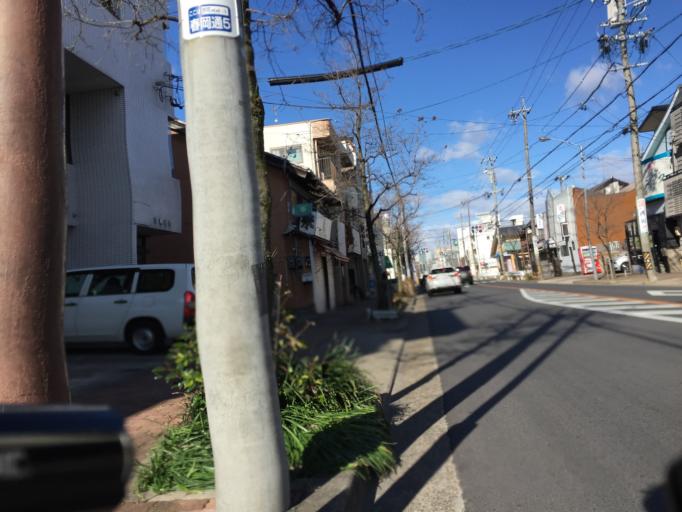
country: JP
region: Aichi
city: Nagoya-shi
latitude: 35.1619
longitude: 136.9412
